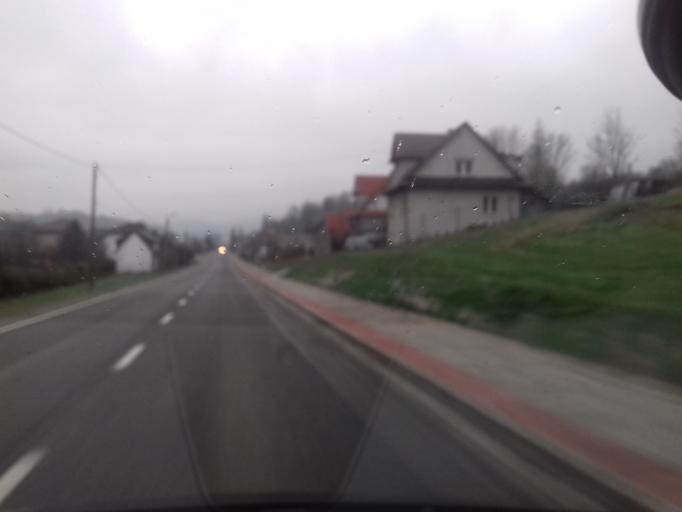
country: PL
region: Lesser Poland Voivodeship
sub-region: Powiat limanowski
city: Mszana Gorna
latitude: 49.6870
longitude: 20.1112
